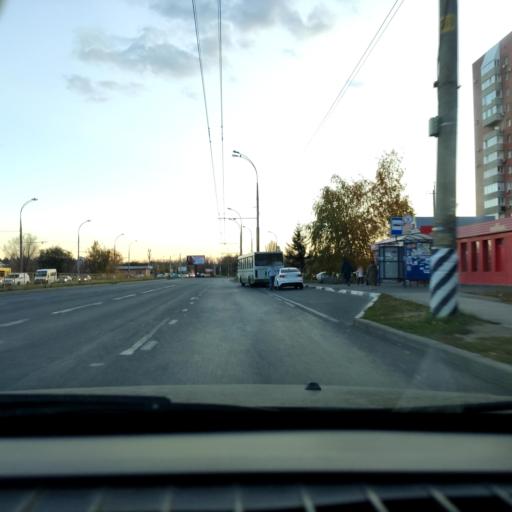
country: RU
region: Samara
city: Tol'yatti
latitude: 53.5003
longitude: 49.2900
